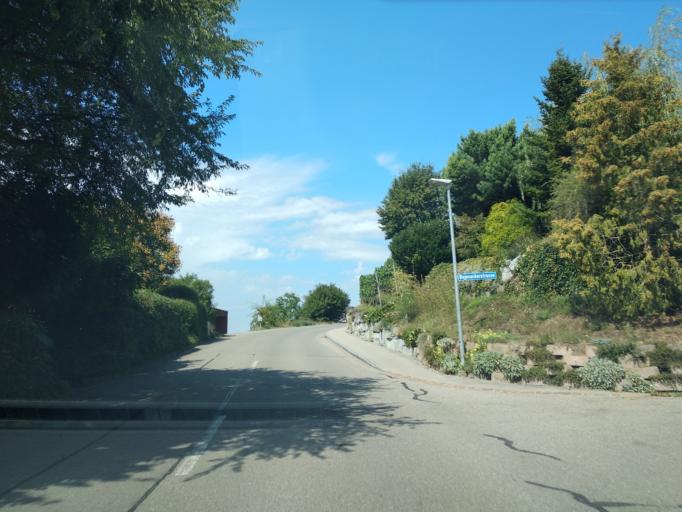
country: CH
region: Thurgau
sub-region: Frauenfeld District
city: Gachnang
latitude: 47.5823
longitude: 8.8300
